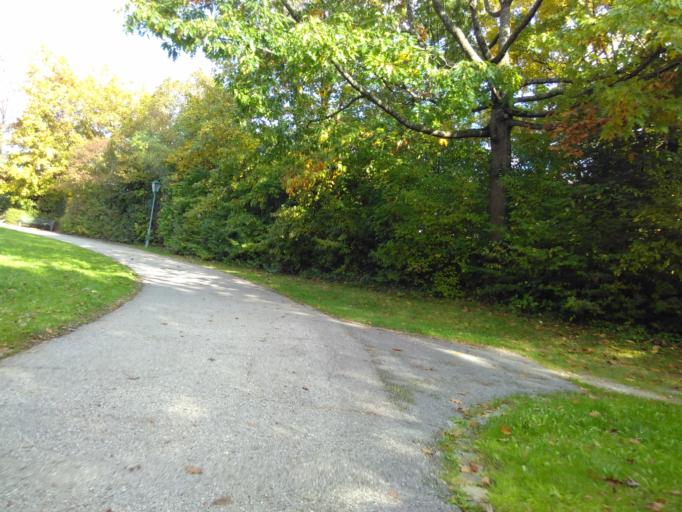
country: DE
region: Bavaria
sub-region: Upper Bavaria
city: Neuried
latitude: 48.1059
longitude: 11.4484
